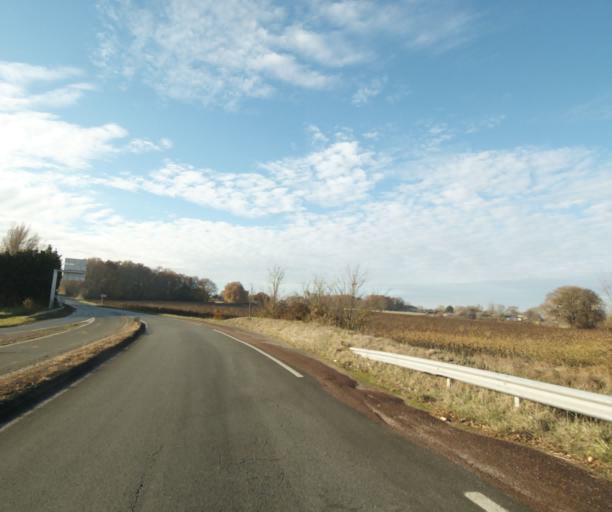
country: FR
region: Poitou-Charentes
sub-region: Departement de la Charente-Maritime
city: Saint-Georges-des-Coteaux
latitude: 45.7452
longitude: -0.6932
